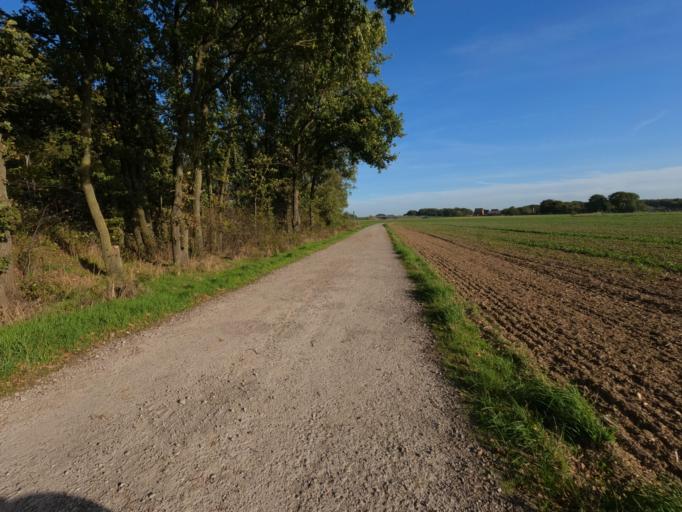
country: DE
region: North Rhine-Westphalia
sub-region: Regierungsbezirk Koln
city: Wassenberg
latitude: 51.1066
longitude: 6.1999
